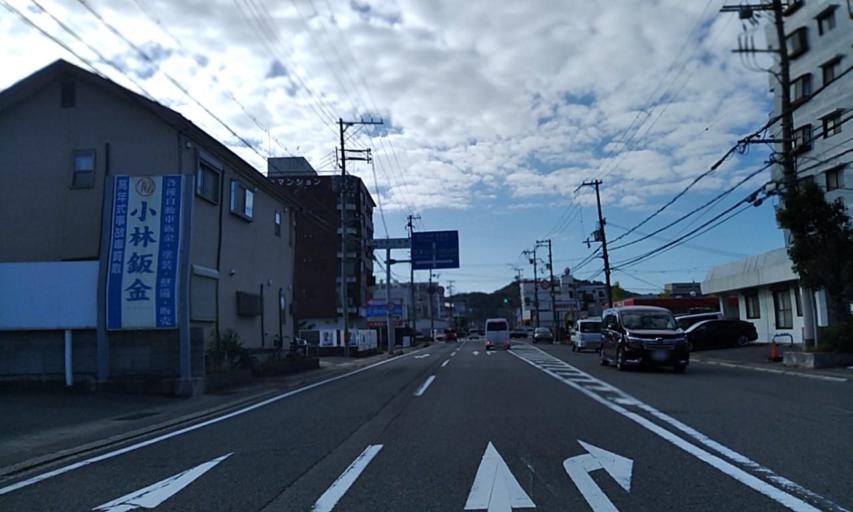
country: JP
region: Wakayama
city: Minato
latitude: 34.2037
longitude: 135.1593
